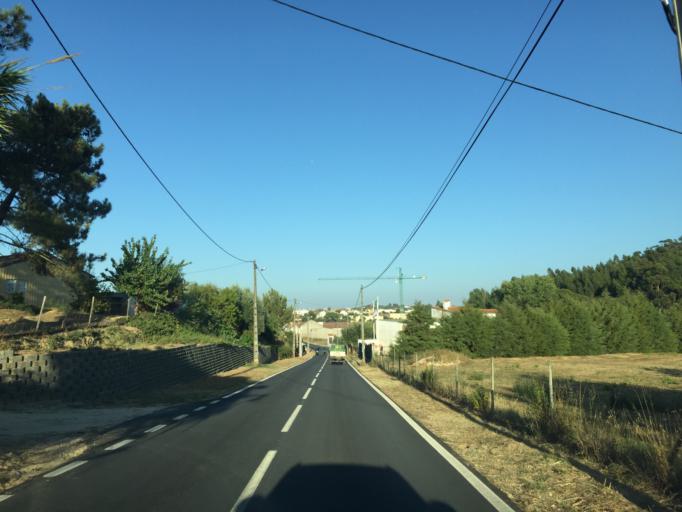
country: PT
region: Lisbon
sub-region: Azambuja
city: Aveiras de Cima
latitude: 39.1403
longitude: -8.9159
